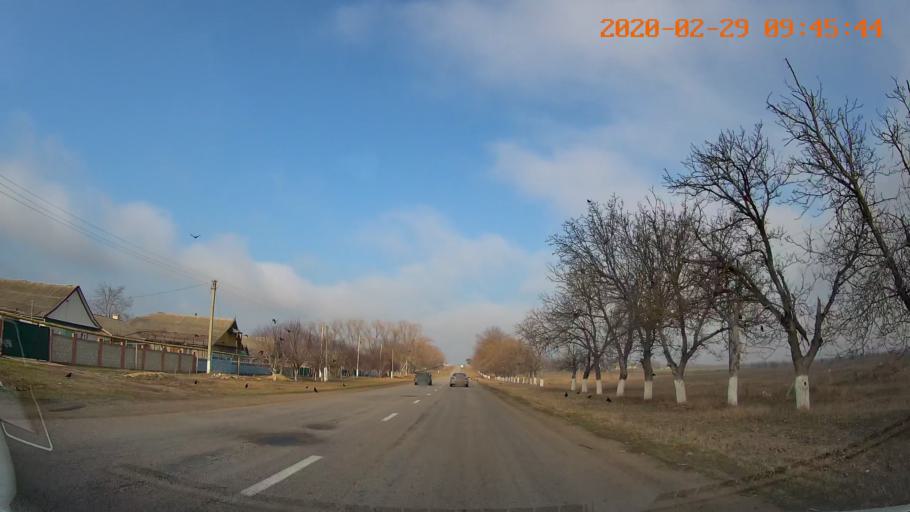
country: MD
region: Telenesti
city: Crasnoe
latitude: 46.6615
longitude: 29.8068
